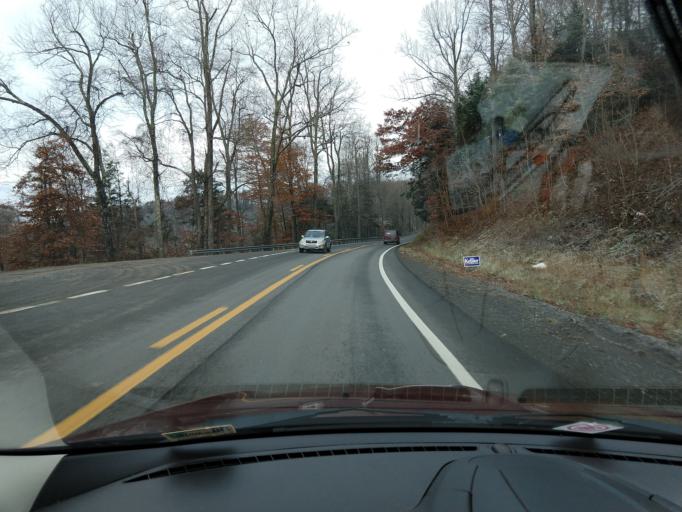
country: US
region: West Virginia
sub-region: Nicholas County
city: Craigsville
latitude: 38.2503
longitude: -80.7243
